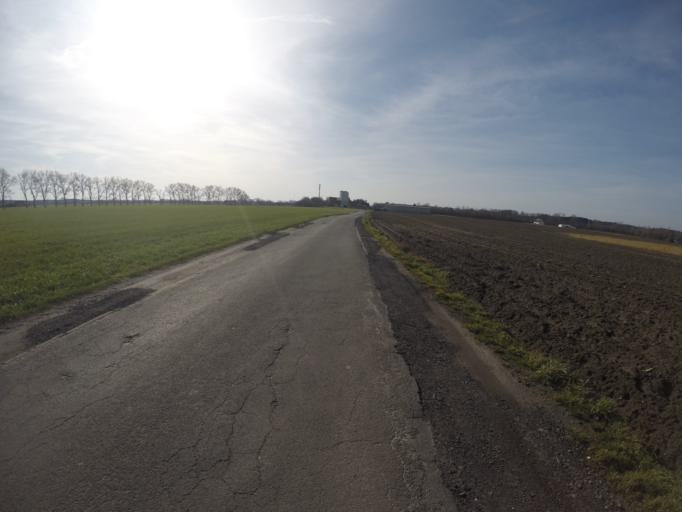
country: BE
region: Flanders
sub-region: Provincie West-Vlaanderen
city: Oostkamp
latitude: 51.1430
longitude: 3.2638
